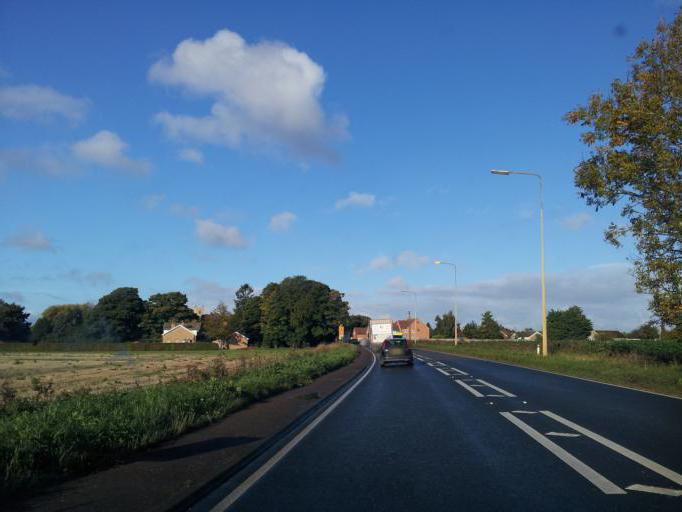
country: GB
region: England
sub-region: Norfolk
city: King's Lynn
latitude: 52.7171
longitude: 0.5088
